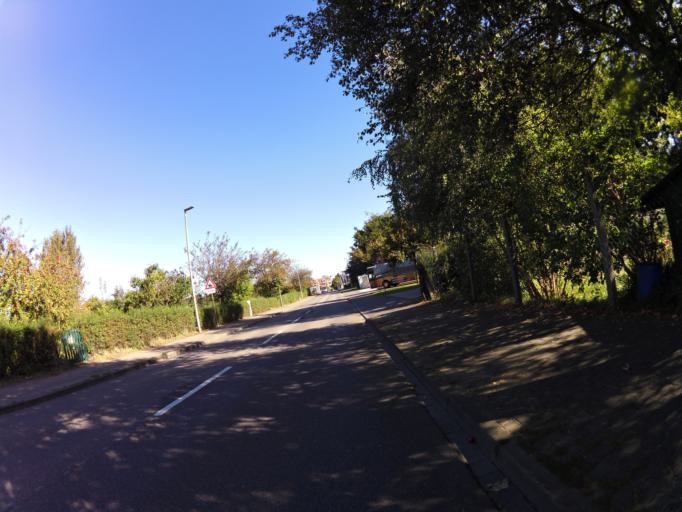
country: DE
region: Schleswig-Holstein
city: Eckernforde
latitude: 54.4698
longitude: 9.8307
